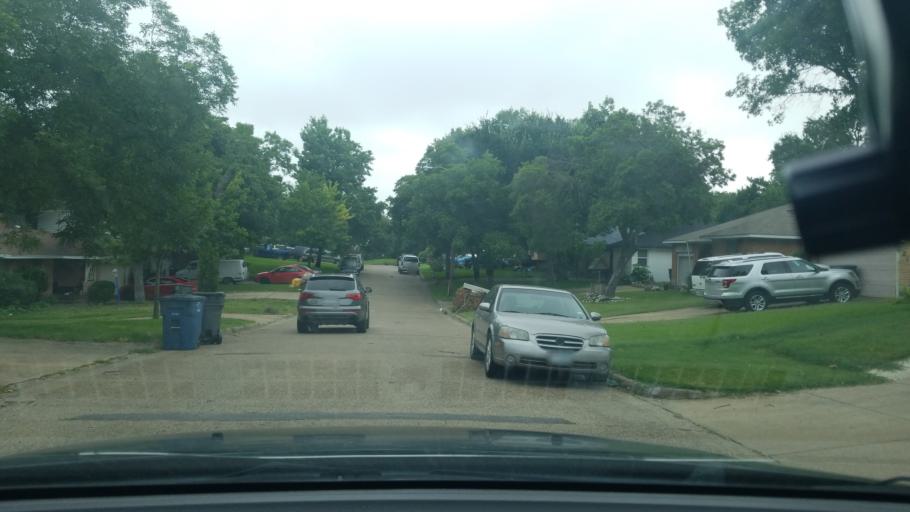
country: US
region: Texas
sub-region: Dallas County
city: Balch Springs
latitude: 32.7677
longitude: -96.6919
